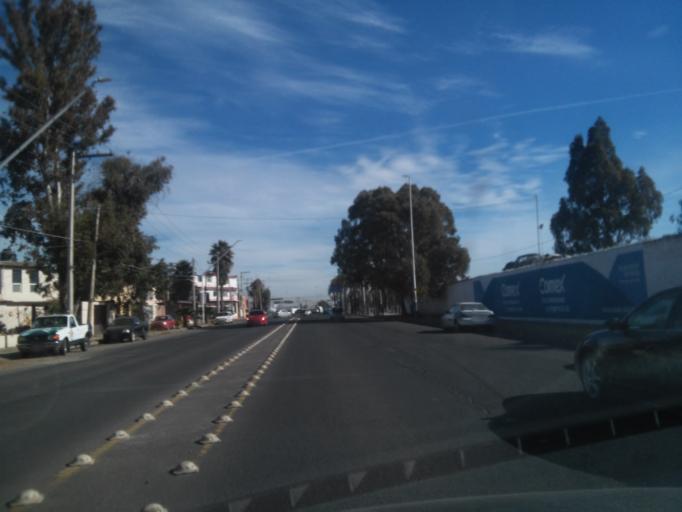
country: MX
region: Durango
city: Victoria de Durango
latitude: 24.0412
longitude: -104.6601
